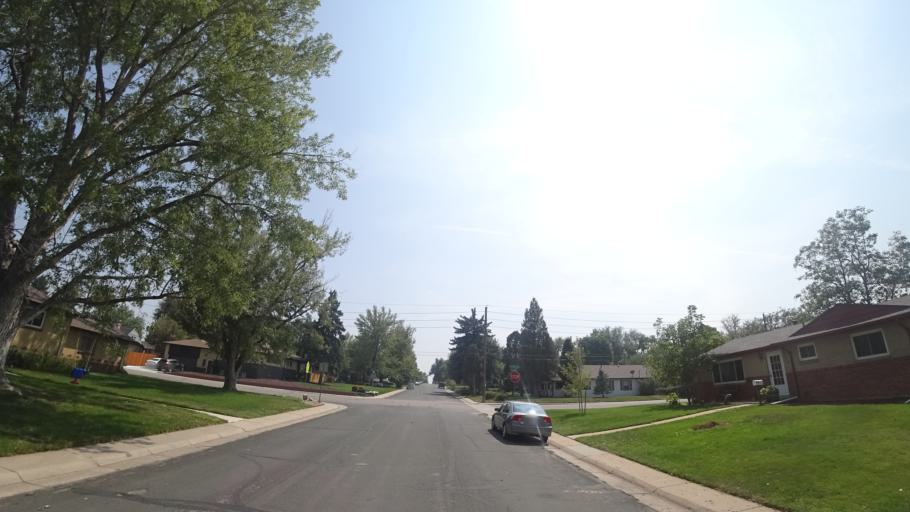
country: US
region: Colorado
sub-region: Arapahoe County
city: Englewood
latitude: 39.6335
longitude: -104.9960
